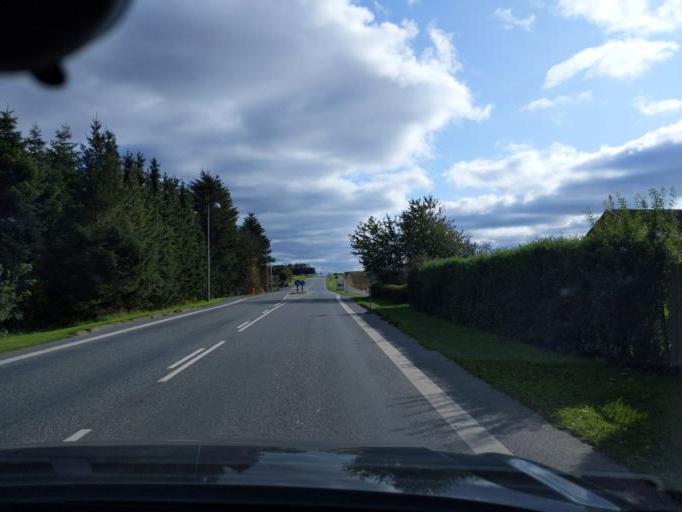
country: DK
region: North Denmark
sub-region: Mariagerfjord Kommune
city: Hobro
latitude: 56.5247
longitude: 9.7299
